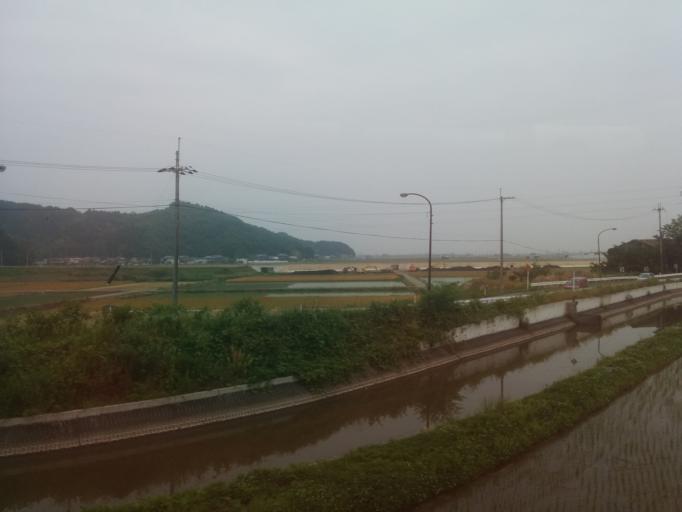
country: JP
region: Shiga Prefecture
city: Omihachiman
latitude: 35.1566
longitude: 136.1490
